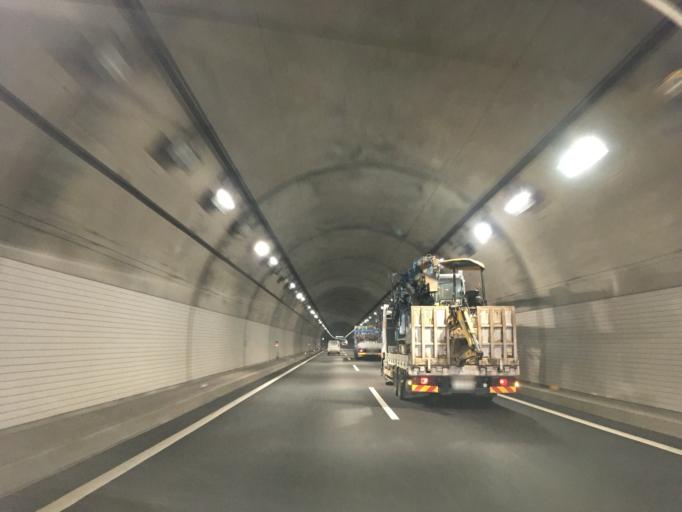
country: JP
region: Kanagawa
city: Zama
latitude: 35.5099
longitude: 139.3638
